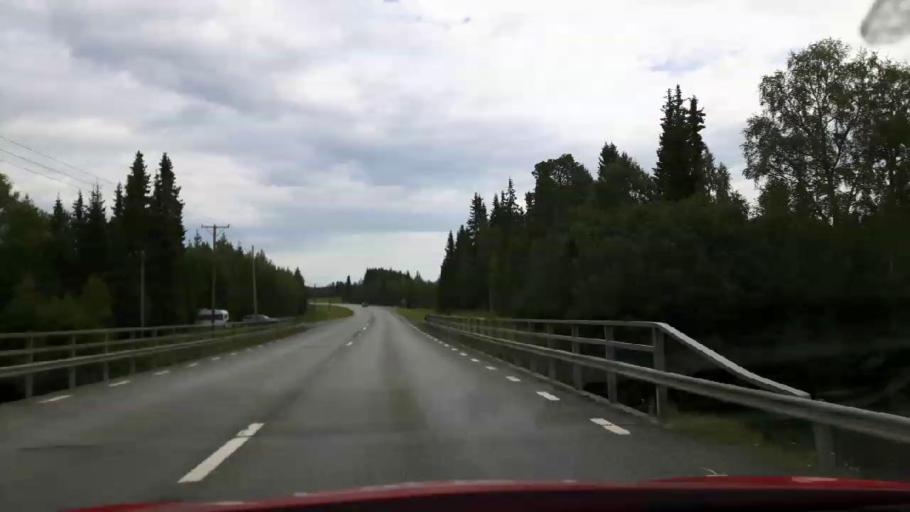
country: SE
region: Jaemtland
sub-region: Stroemsunds Kommun
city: Stroemsund
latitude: 63.6393
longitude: 15.3664
